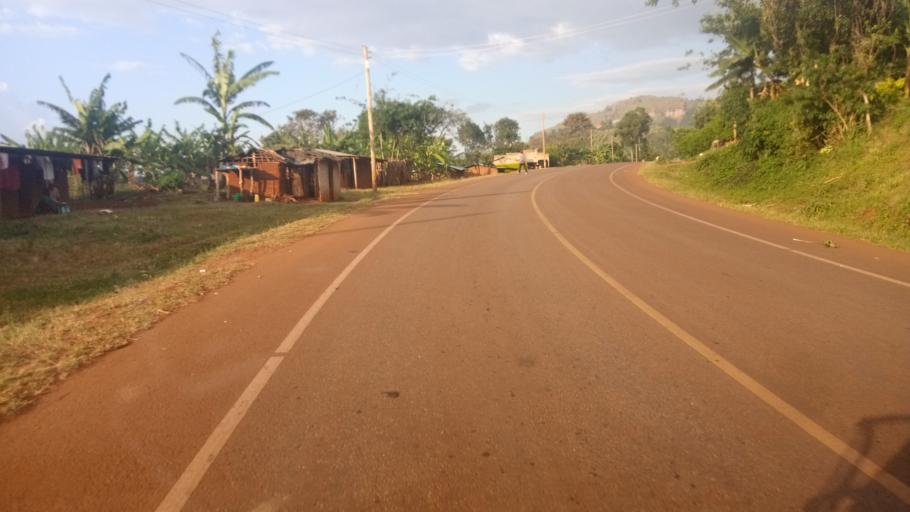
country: UG
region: Eastern Region
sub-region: Sironko District
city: Sironko
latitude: 1.3211
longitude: 34.3435
